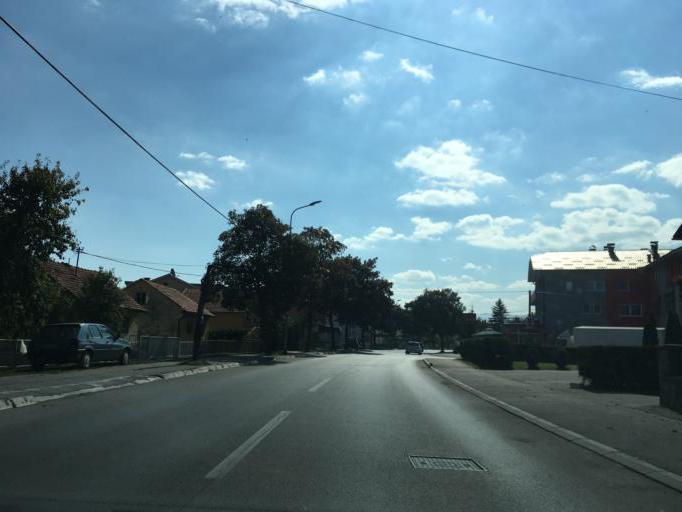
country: BA
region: Federation of Bosnia and Herzegovina
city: Bugojno
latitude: 44.0659
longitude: 17.4503
